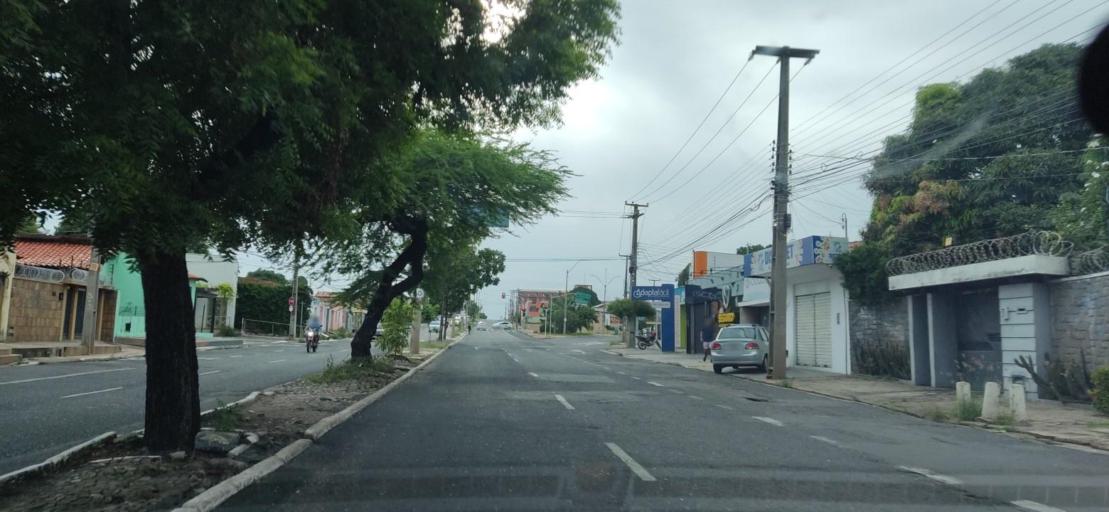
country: BR
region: Piaui
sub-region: Teresina
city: Teresina
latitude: -5.0955
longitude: -42.7937
